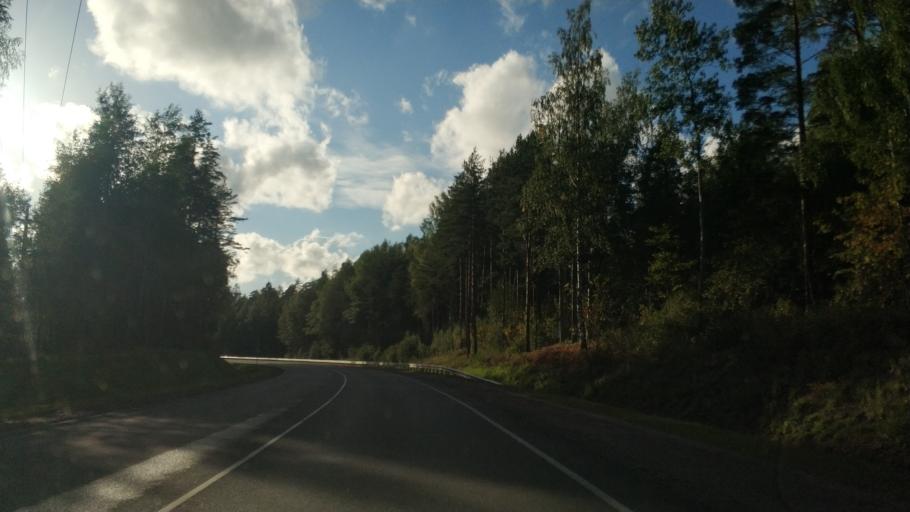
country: RU
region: Leningrad
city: Sapernoye
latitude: 60.7154
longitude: 30.0112
